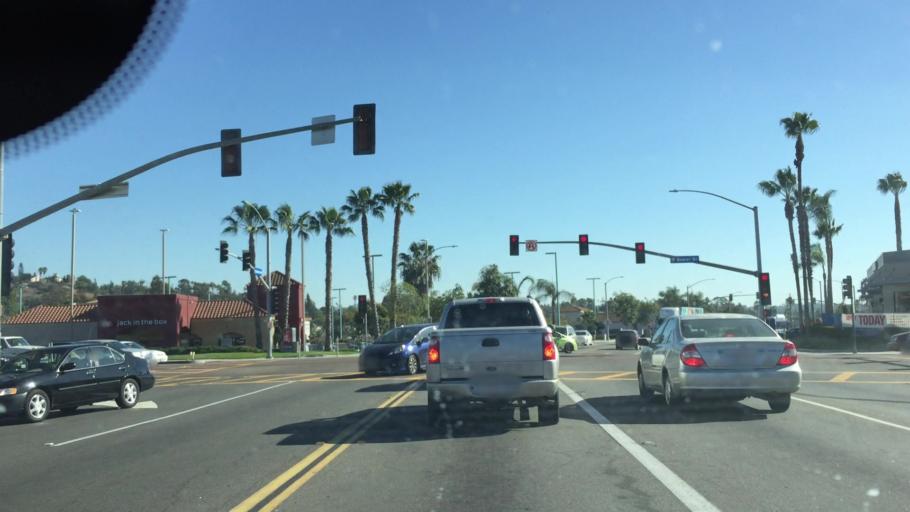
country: US
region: California
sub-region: San Diego County
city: Vista
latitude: 33.2215
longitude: -117.2452
